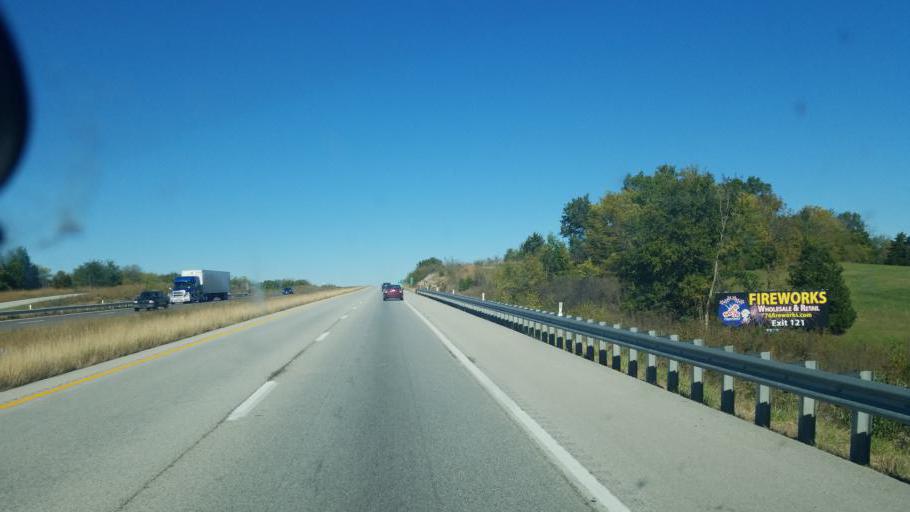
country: US
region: Missouri
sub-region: Cooper County
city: Boonville
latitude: 38.9385
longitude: -92.9829
